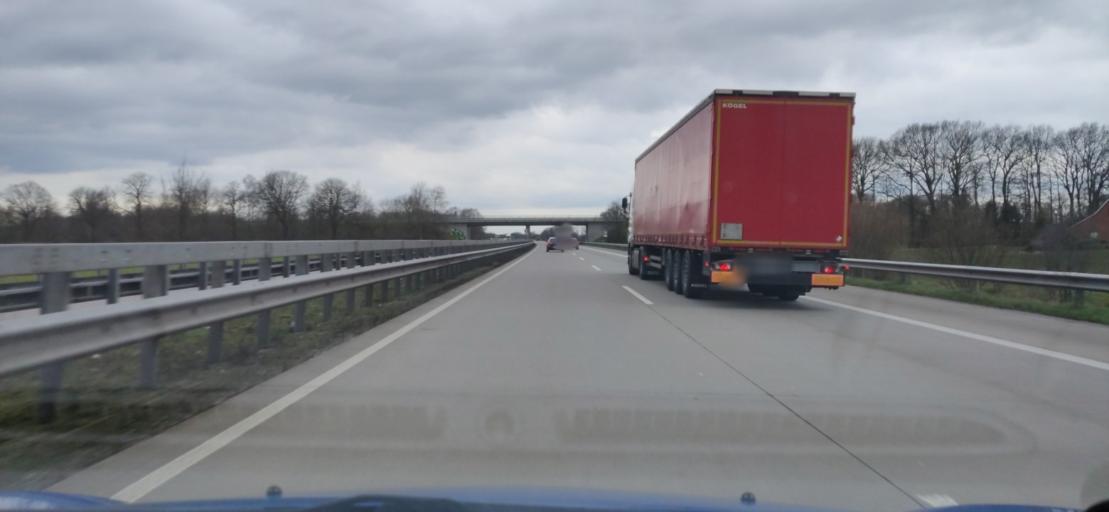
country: DE
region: Lower Saxony
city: Quendorf
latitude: 52.3440
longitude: 7.1997
